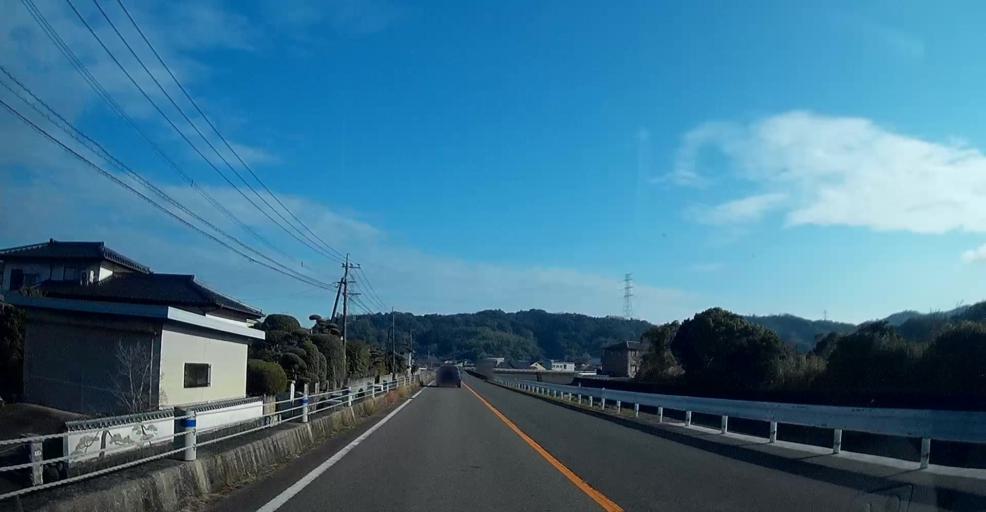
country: JP
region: Kumamoto
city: Yatsushiro
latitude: 32.5202
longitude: 130.4459
